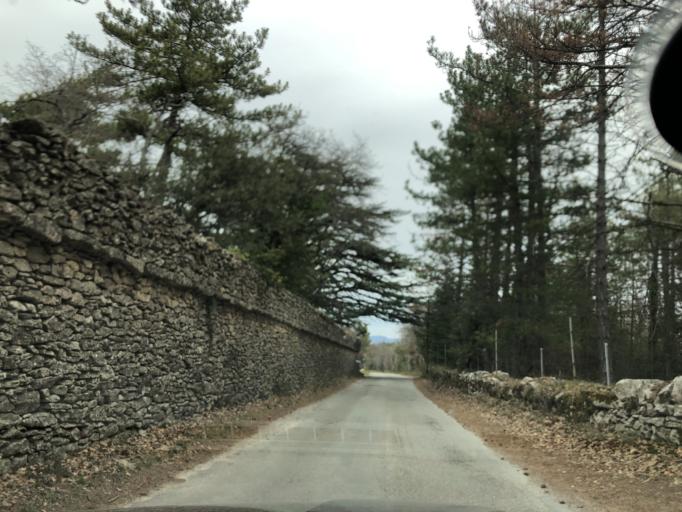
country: FR
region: Provence-Alpes-Cote d'Azur
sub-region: Departement du Vaucluse
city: Bonnieux
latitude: 43.8122
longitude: 5.3171
